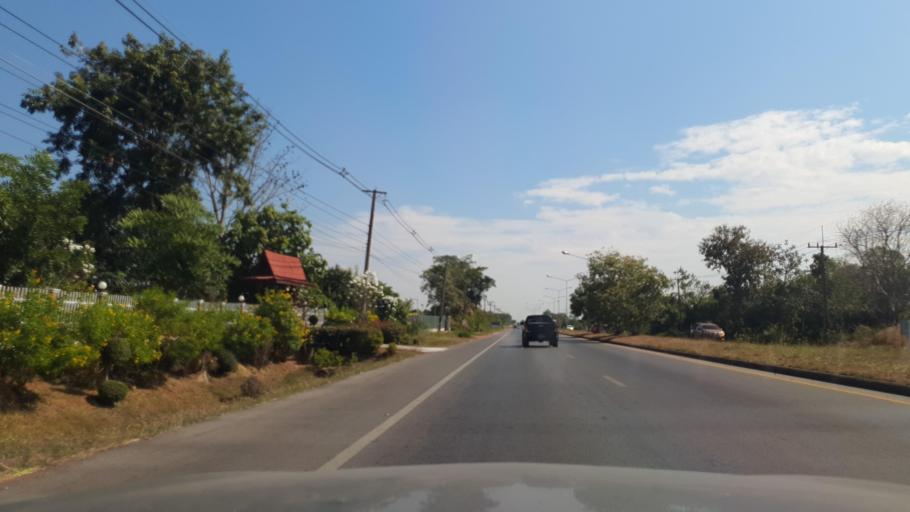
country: TH
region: Maha Sarakham
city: Chiang Yuen
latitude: 16.3726
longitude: 103.1435
